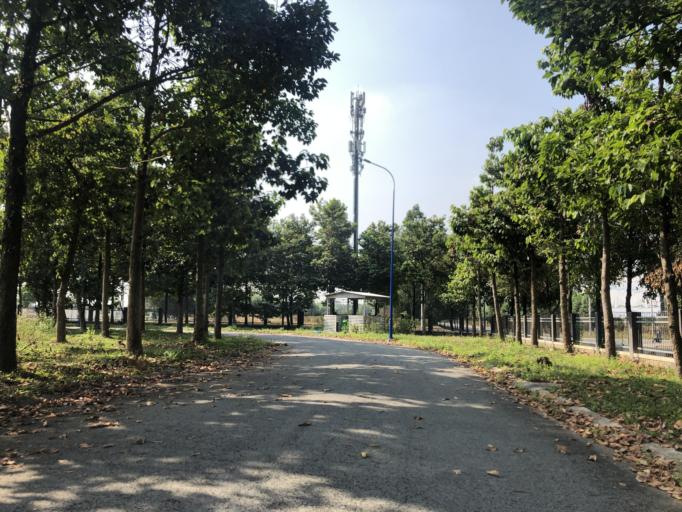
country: VN
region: Binh Duong
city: Thu Dau Mot
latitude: 11.0519
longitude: 106.6635
